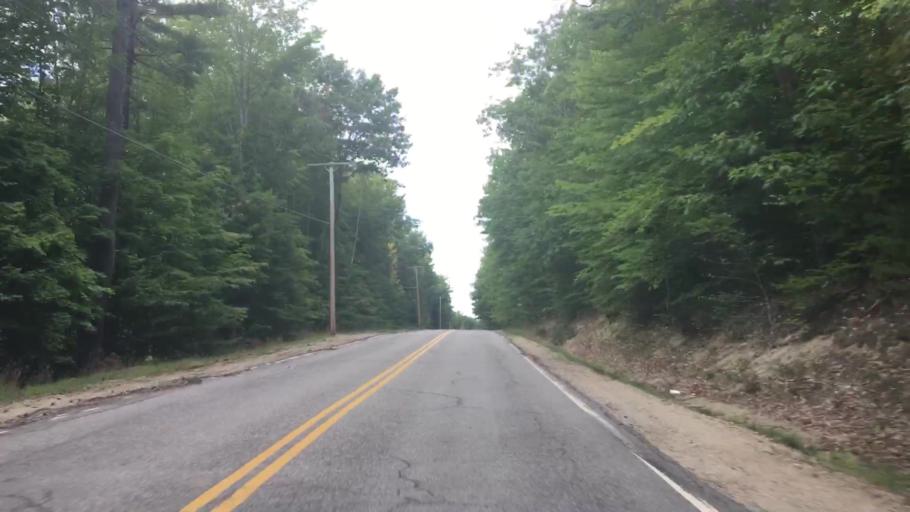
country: US
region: Maine
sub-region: Oxford County
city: Oxford
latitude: 44.0226
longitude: -70.5290
